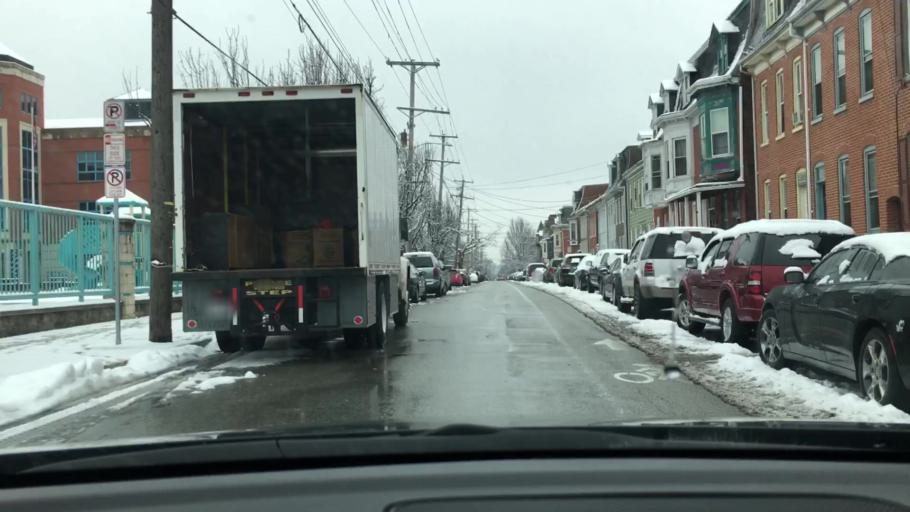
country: US
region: Pennsylvania
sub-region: York County
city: West York
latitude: 39.9564
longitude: -76.7421
